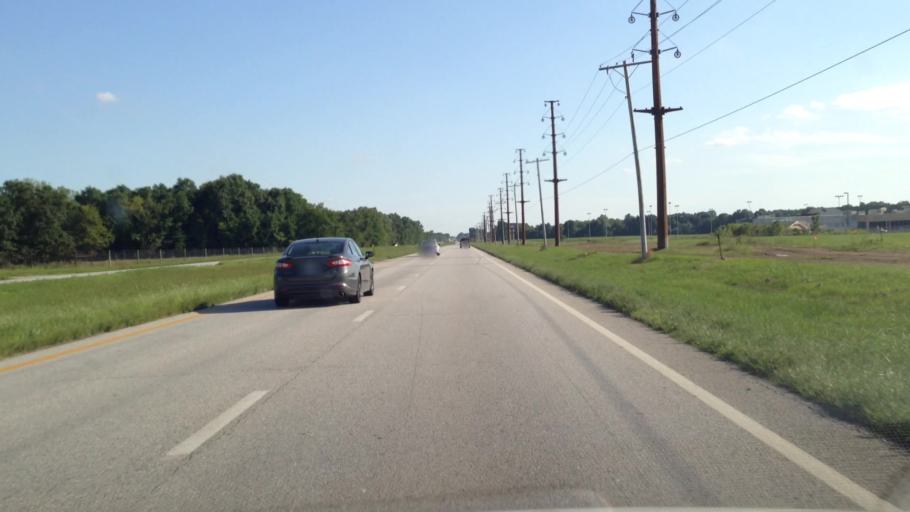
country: US
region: Kansas
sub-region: Crawford County
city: Frontenac
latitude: 37.4826
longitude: -94.7053
